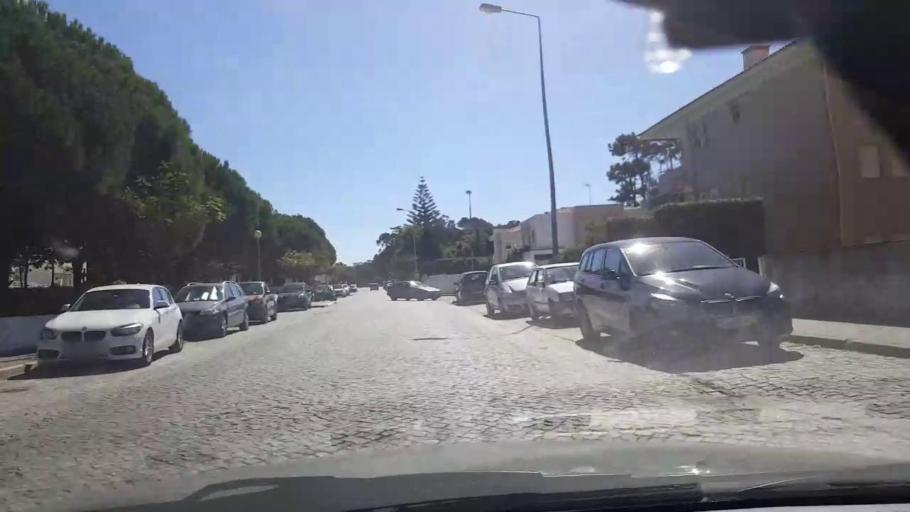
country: PT
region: Porto
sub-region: Vila do Conde
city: Arvore
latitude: 41.3344
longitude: -8.7320
